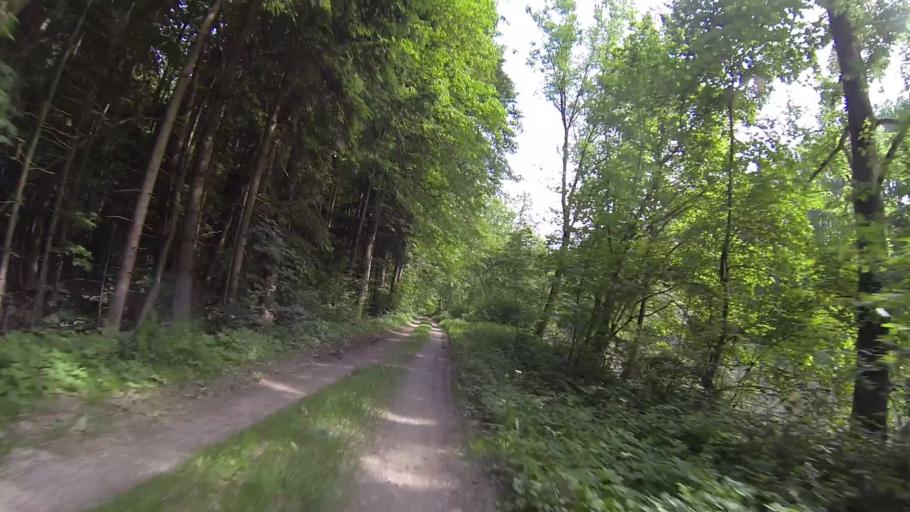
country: DE
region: Bavaria
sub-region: Swabia
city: Neu-Ulm
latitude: 48.3546
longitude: 9.9974
